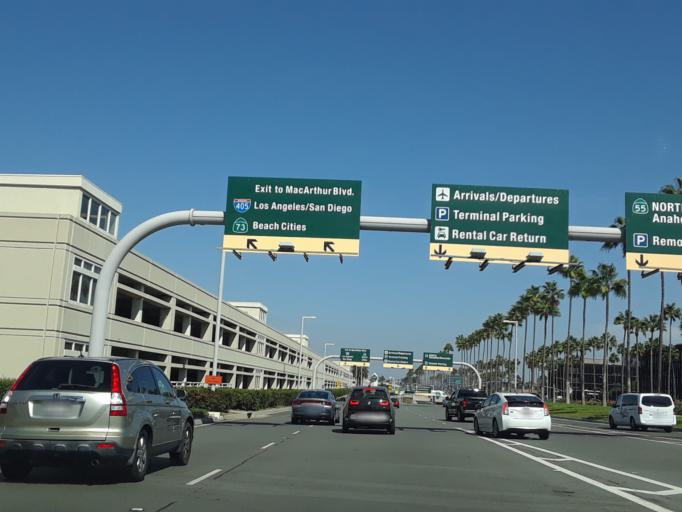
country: US
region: California
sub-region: Orange County
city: Irvine
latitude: 33.6763
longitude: -117.8614
